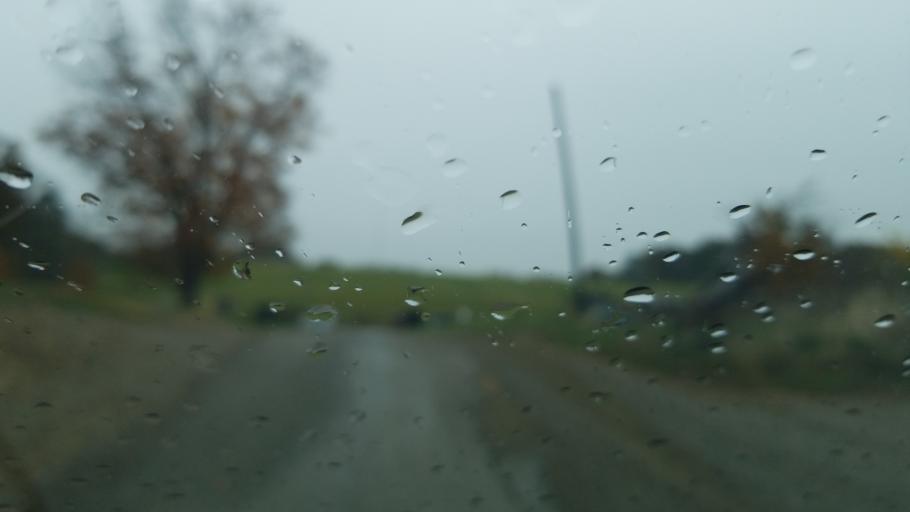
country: US
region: Ohio
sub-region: Coshocton County
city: Coshocton
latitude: 40.4034
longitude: -81.8644
